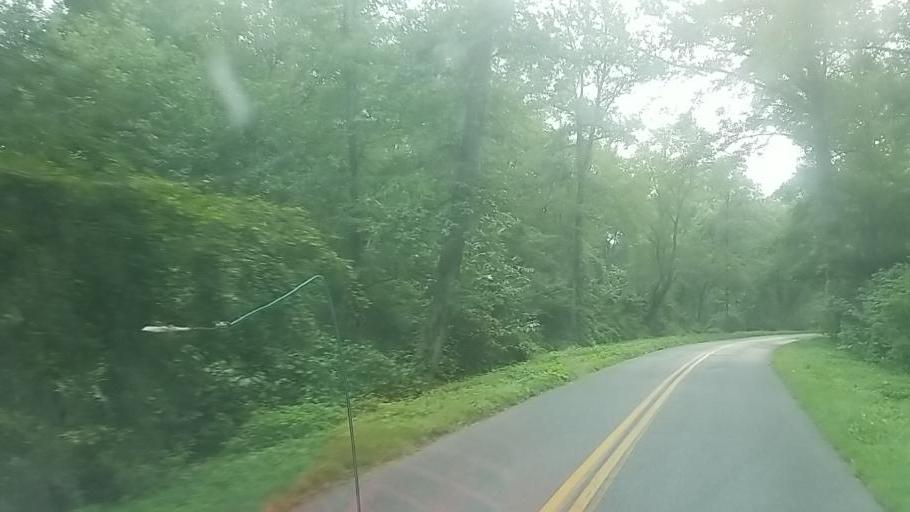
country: US
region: Maryland
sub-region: Wicomico County
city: Pittsville
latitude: 38.4410
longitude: -75.3350
